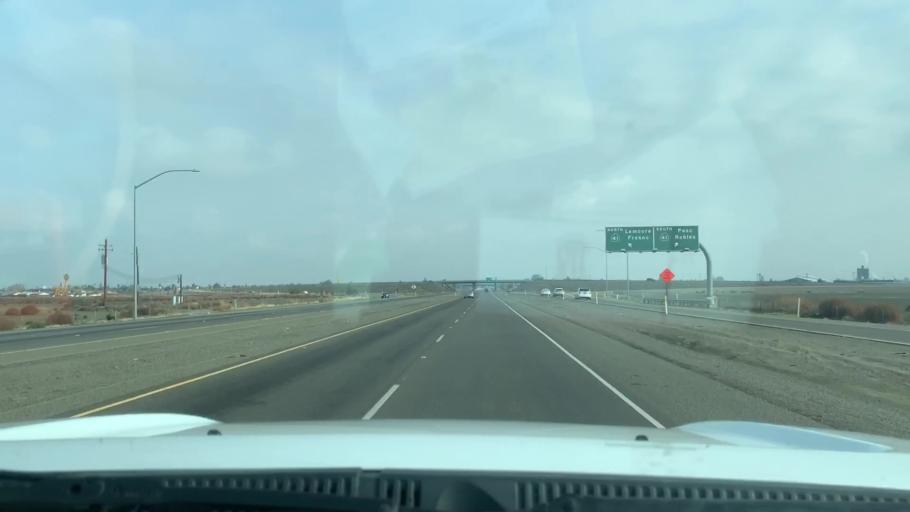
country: US
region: California
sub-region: Kings County
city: Lemoore
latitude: 36.2800
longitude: -119.8131
